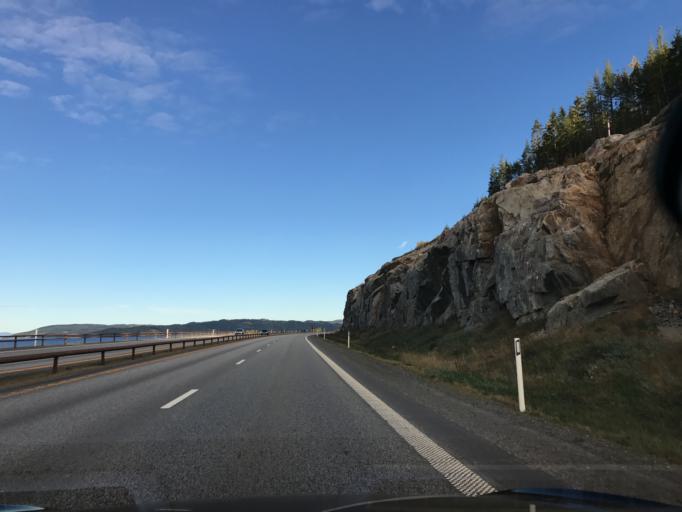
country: NO
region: Hedmark
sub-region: Stange
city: Stange
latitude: 60.5464
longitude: 11.2474
